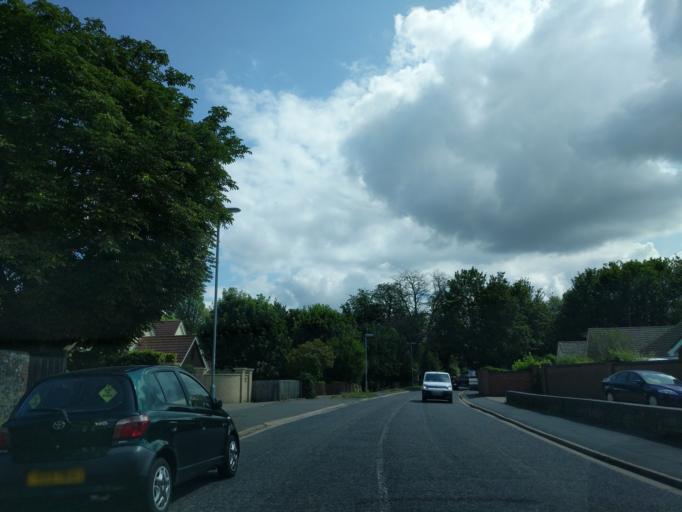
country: GB
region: England
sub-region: Cambridgeshire
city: Isleham
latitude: 52.3117
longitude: 0.3879
